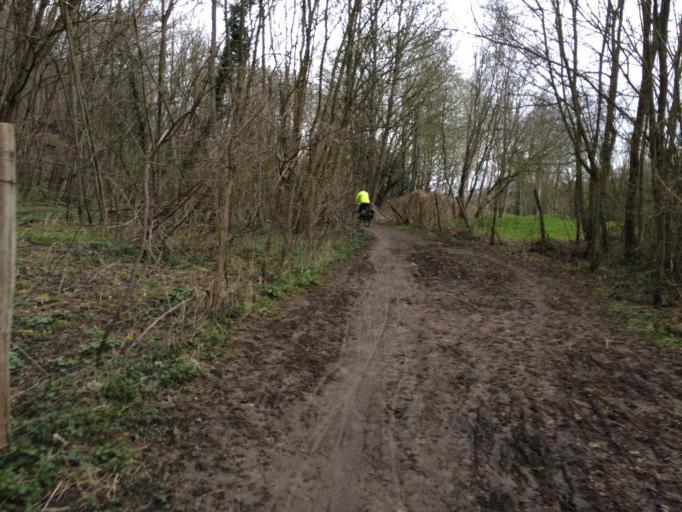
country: FR
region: Ile-de-France
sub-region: Departement des Yvelines
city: Les Loges-en-Josas
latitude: 48.7581
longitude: 2.1505
